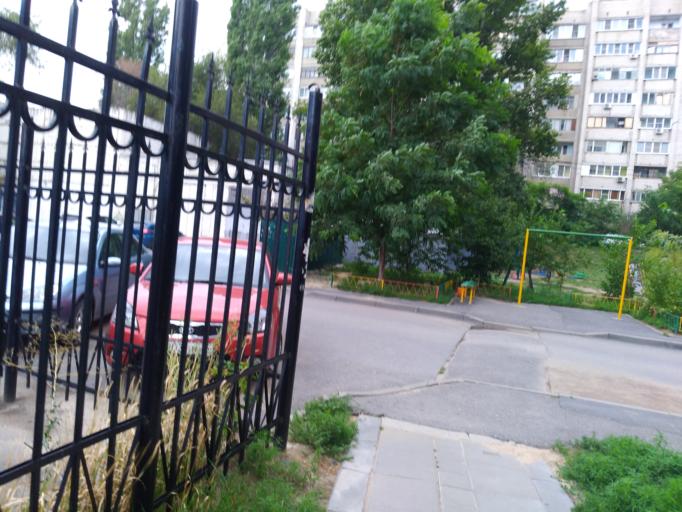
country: RU
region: Volgograd
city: Volgograd
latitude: 48.7240
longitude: 44.5256
